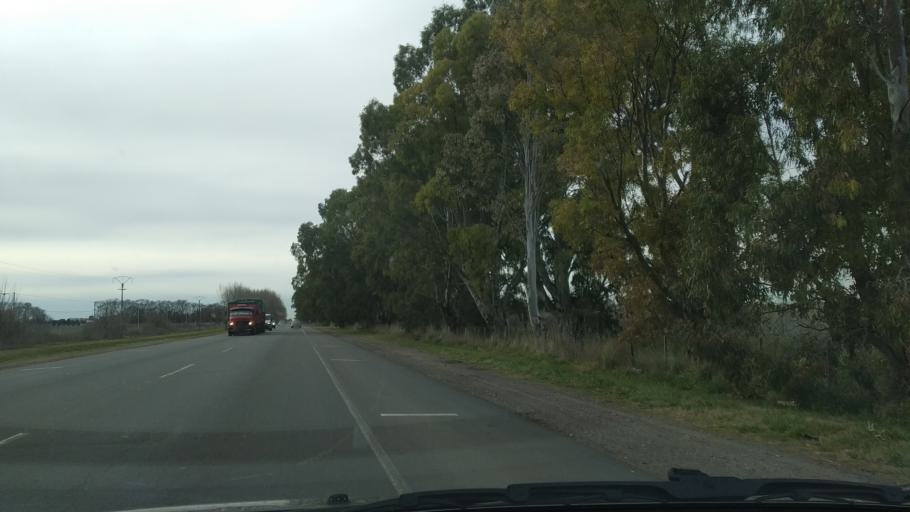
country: AR
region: Buenos Aires
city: Olavarria
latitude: -36.9717
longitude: -60.2742
